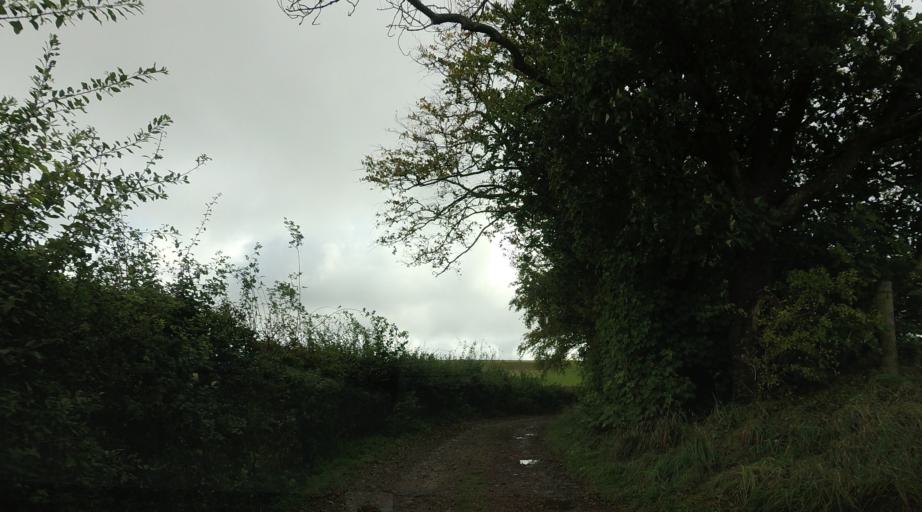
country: GB
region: Scotland
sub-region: Fife
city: Balmullo
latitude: 56.3751
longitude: -2.9557
